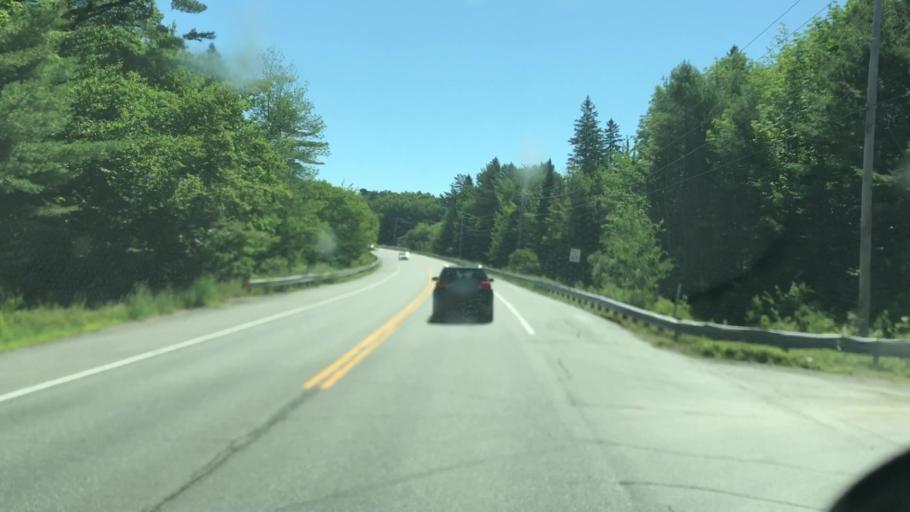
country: US
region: Maine
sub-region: Penobscot County
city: Holden
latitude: 44.7548
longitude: -68.6816
